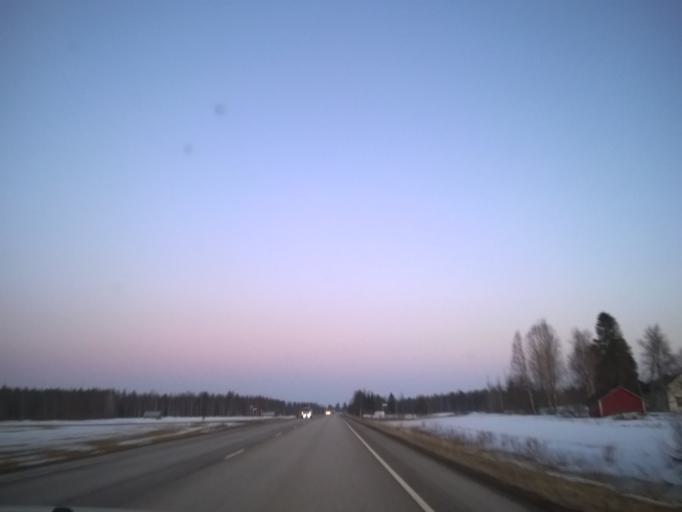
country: FI
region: Northern Ostrobothnia
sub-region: Nivala-Haapajaervi
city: Kaersaemaeki
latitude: 63.8331
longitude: 25.8677
